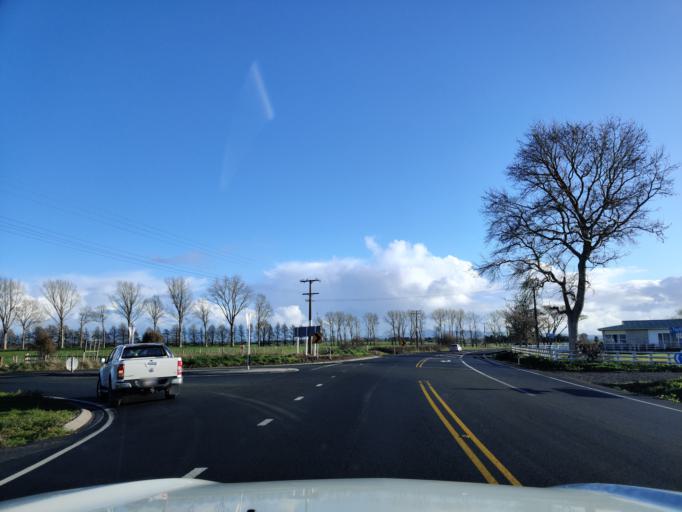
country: NZ
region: Waikato
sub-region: Hauraki District
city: Paeroa
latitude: -37.4892
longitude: 175.6072
